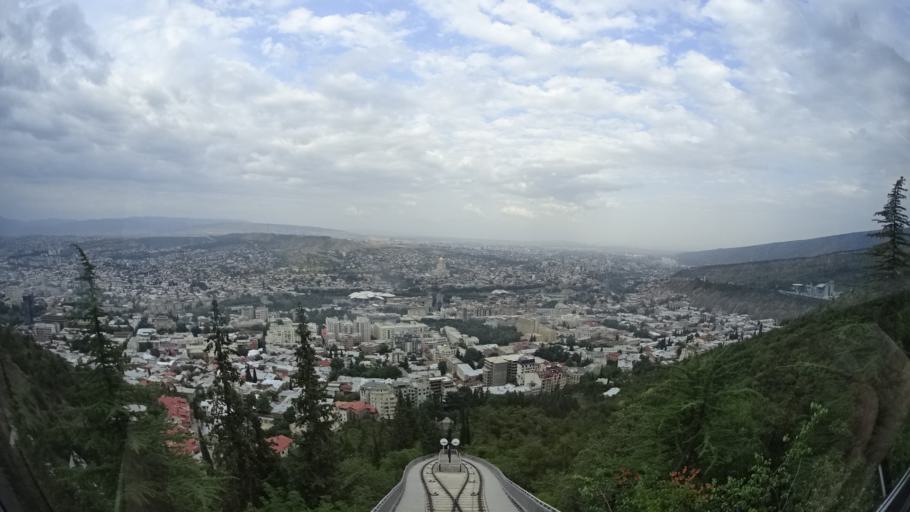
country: GE
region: T'bilisi
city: Tbilisi
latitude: 41.6951
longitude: 44.7886
